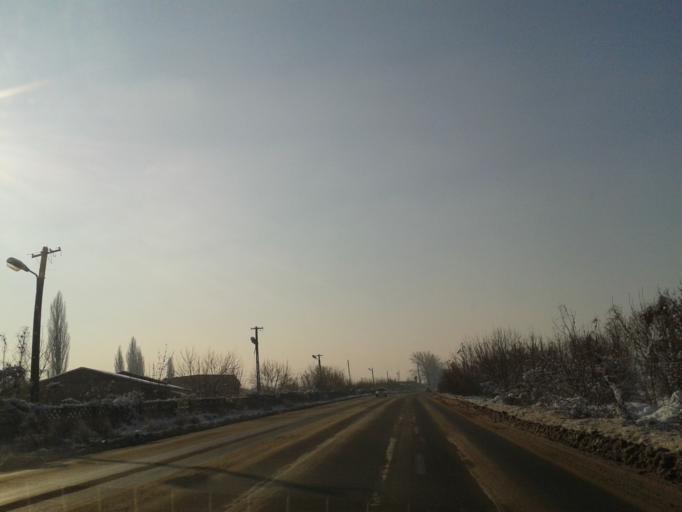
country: RO
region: Hunedoara
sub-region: Municipiul Hunedoara
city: Pestisu Mare
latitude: 45.8129
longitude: 22.9323
